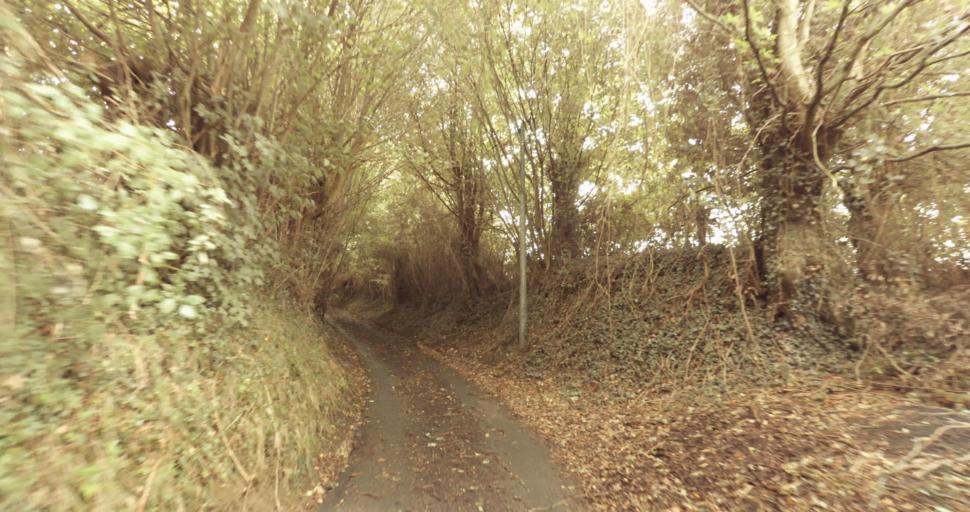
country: FR
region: Lower Normandy
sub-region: Departement de l'Orne
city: Vimoutiers
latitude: 48.8782
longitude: 0.1844
